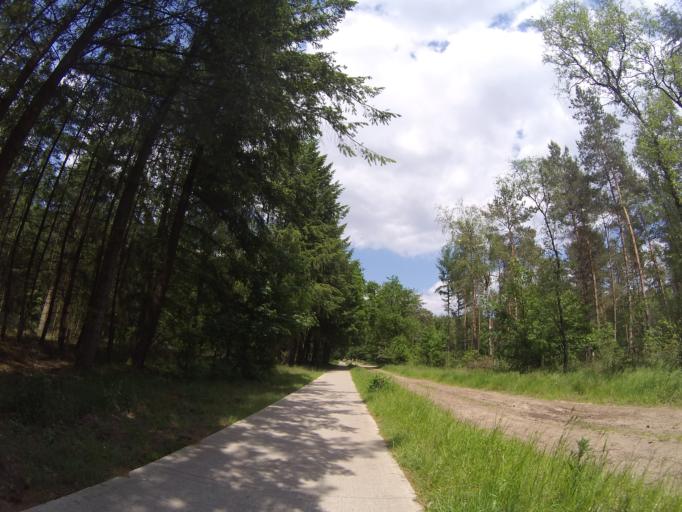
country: NL
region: Gelderland
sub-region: Gemeente Ede
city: Harskamp
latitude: 52.1775
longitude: 5.7636
